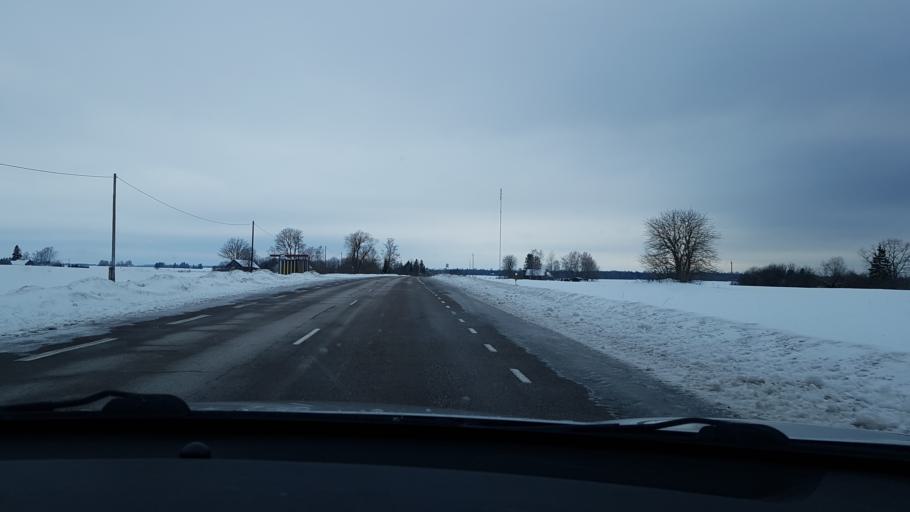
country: EE
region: Jaervamaa
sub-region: Jaerva-Jaani vald
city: Jarva-Jaani
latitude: 58.9176
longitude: 25.8721
